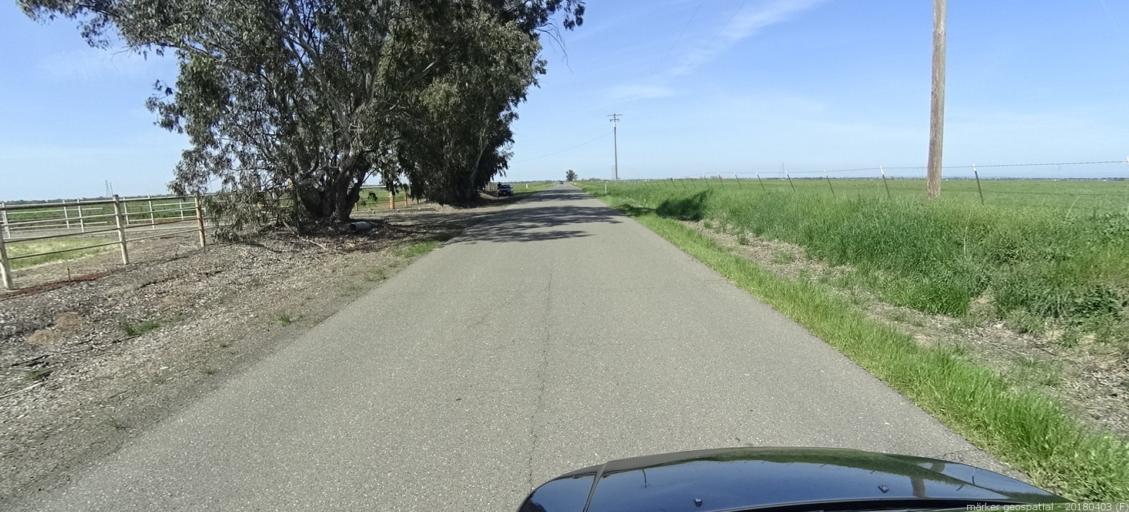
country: US
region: California
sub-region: Sacramento County
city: Herald
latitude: 38.3399
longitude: -121.2976
